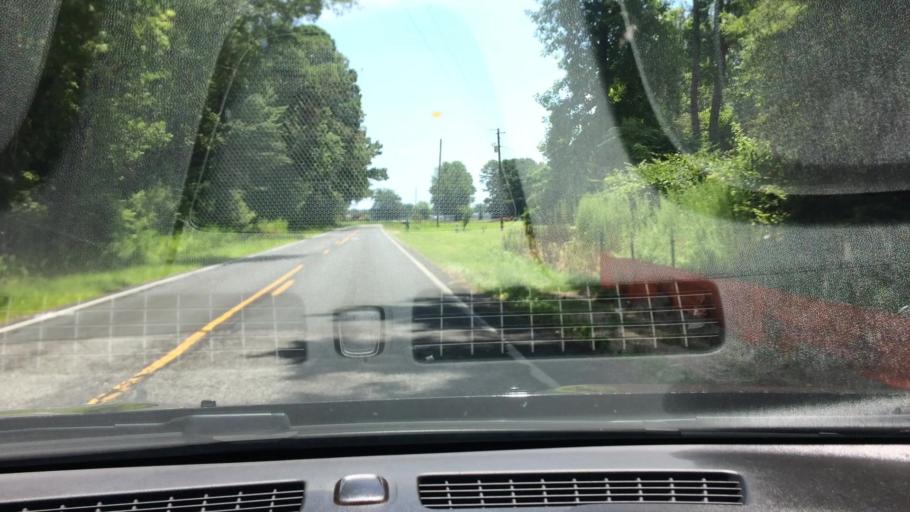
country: US
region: North Carolina
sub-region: Beaufort County
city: Washington
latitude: 35.5978
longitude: -77.1516
